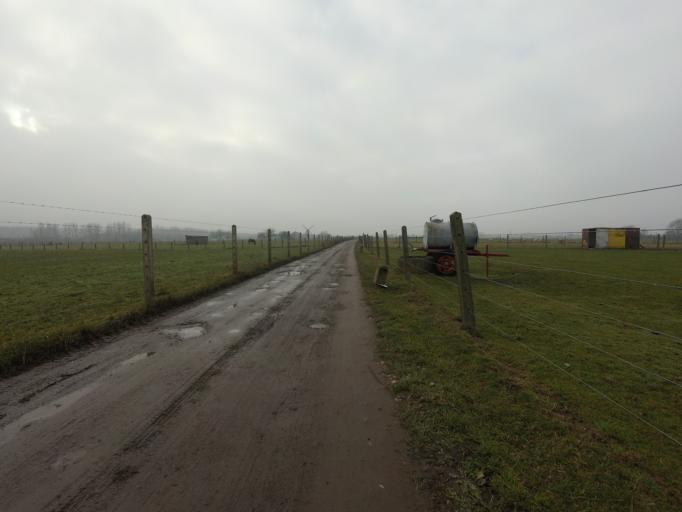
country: BE
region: Flanders
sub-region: Provincie Oost-Vlaanderen
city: Ninove
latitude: 50.8214
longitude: 3.9837
